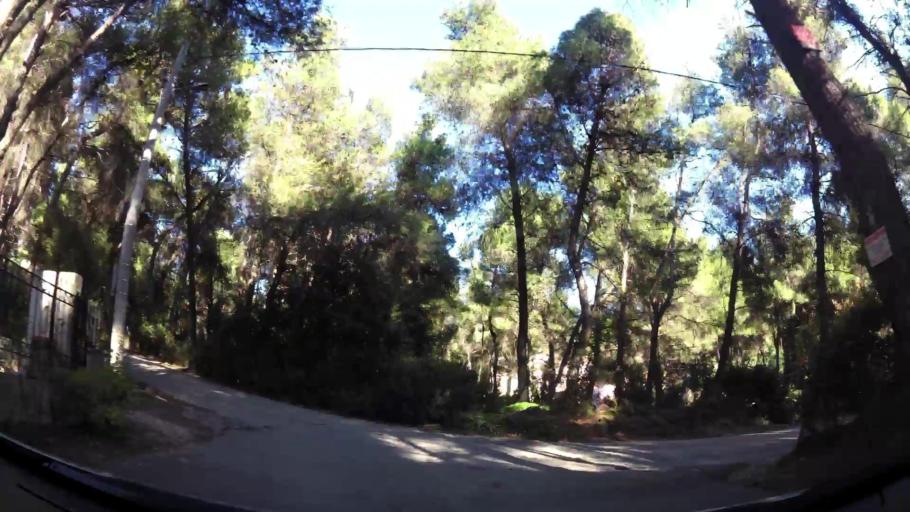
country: GR
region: Attica
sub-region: Nomarchia Athinas
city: Ekali
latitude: 38.1205
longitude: 23.8445
